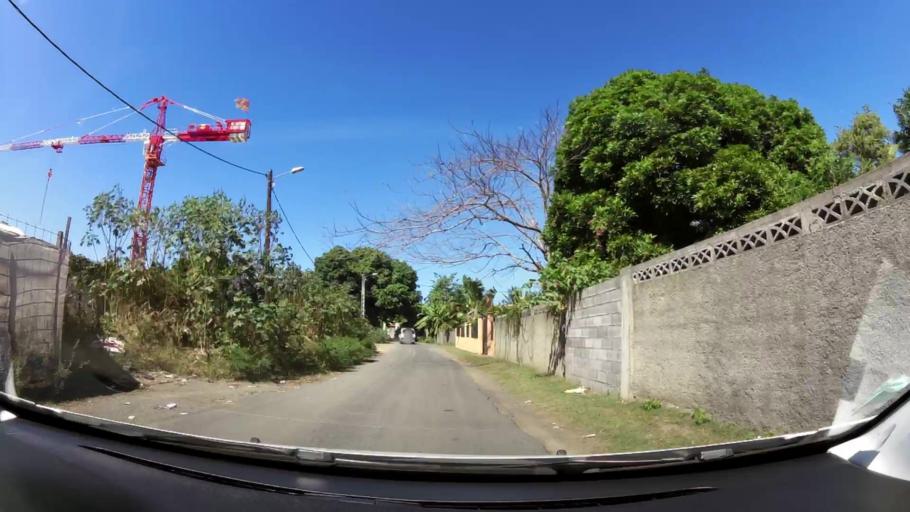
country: YT
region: Pamandzi
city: Pamandzi
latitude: -12.7959
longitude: 45.2768
